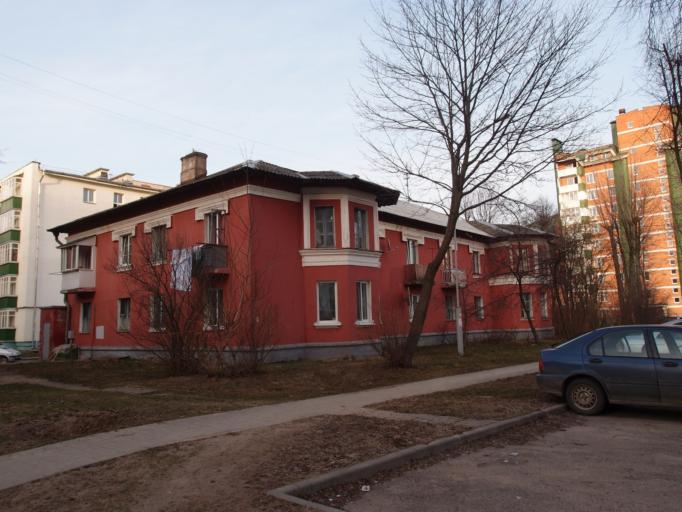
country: BY
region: Minsk
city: Minsk
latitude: 53.9274
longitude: 27.5972
